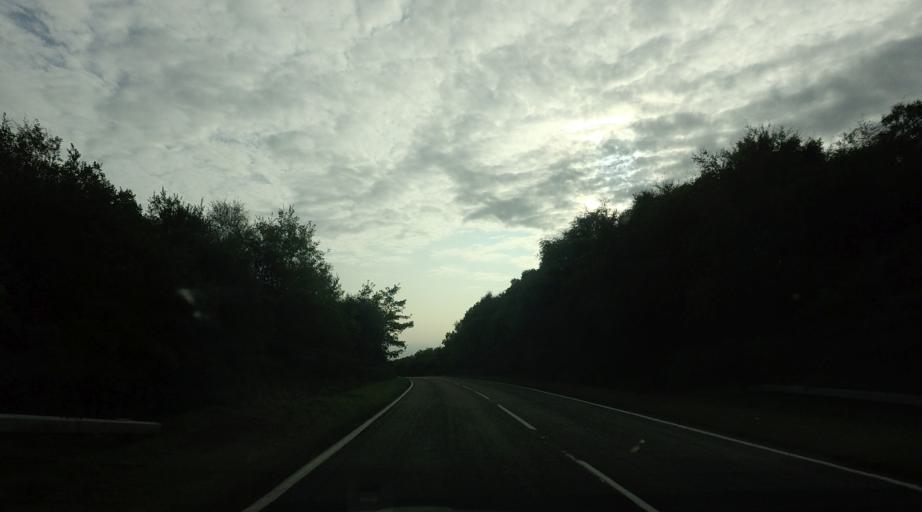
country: GB
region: Scotland
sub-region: Highland
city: Brora
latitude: 58.0583
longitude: -3.8075
